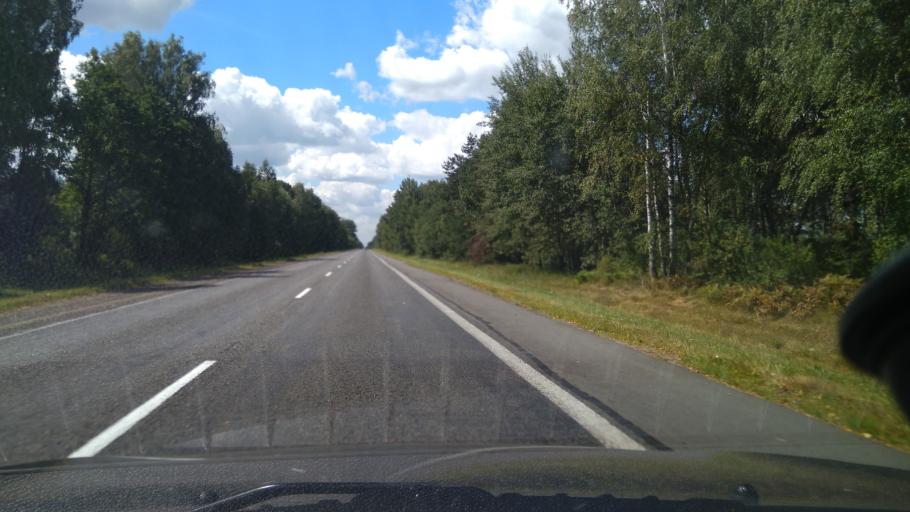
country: BY
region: Brest
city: Ivatsevichy
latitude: 52.6792
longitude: 25.2768
